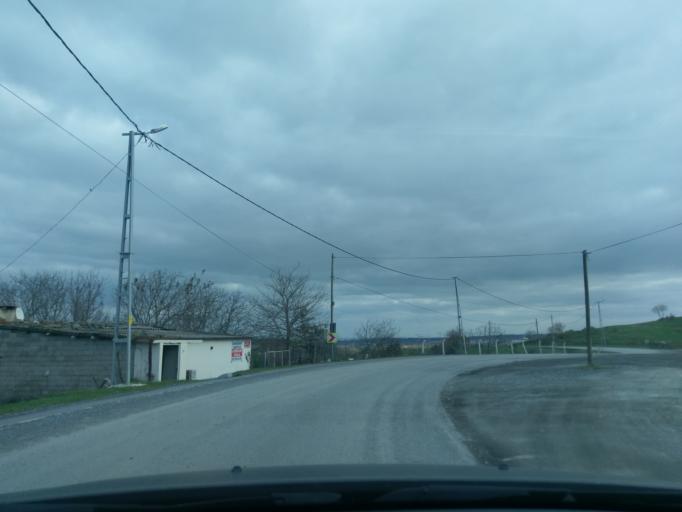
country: TR
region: Istanbul
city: Durusu
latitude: 41.2731
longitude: 28.6931
